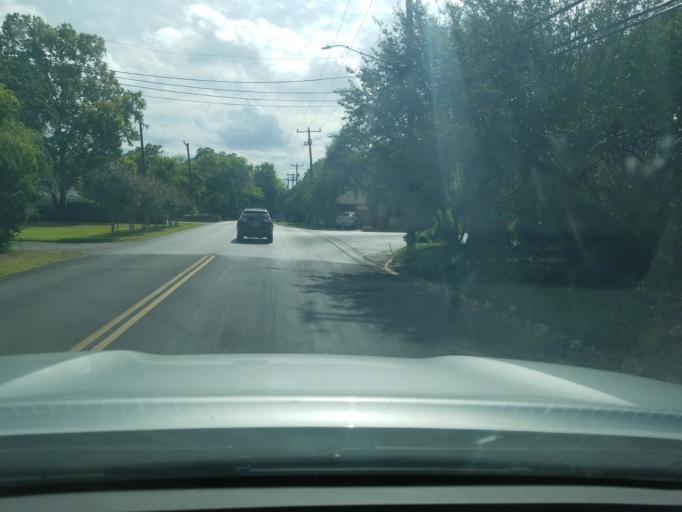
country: US
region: Texas
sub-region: Bexar County
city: Terrell Hills
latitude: 29.4686
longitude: -98.4469
